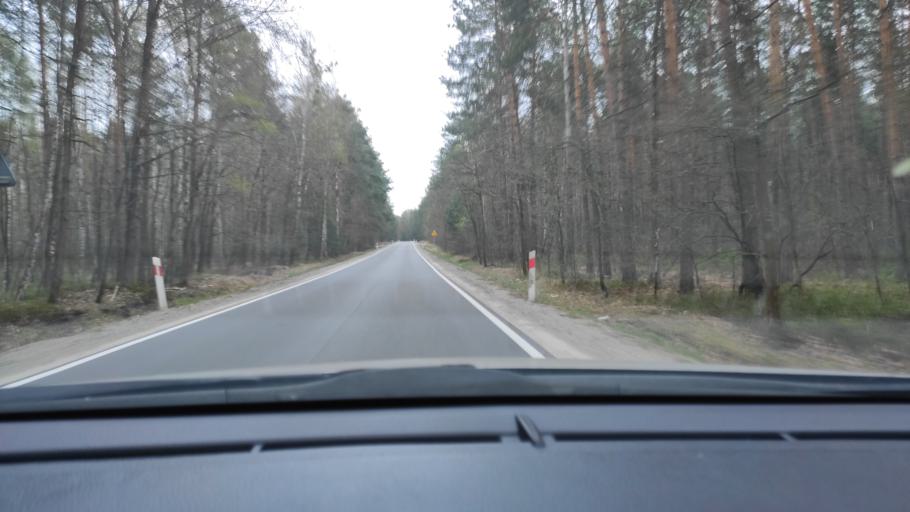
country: PL
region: Masovian Voivodeship
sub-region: Powiat zwolenski
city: Zwolen
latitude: 51.4109
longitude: 21.5159
